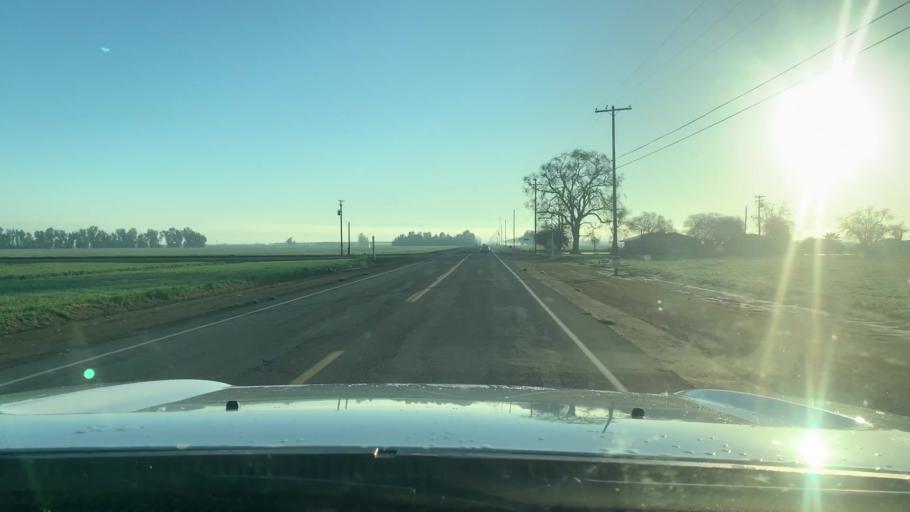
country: US
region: California
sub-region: Kings County
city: Home Garden
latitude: 36.2112
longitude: -119.6292
